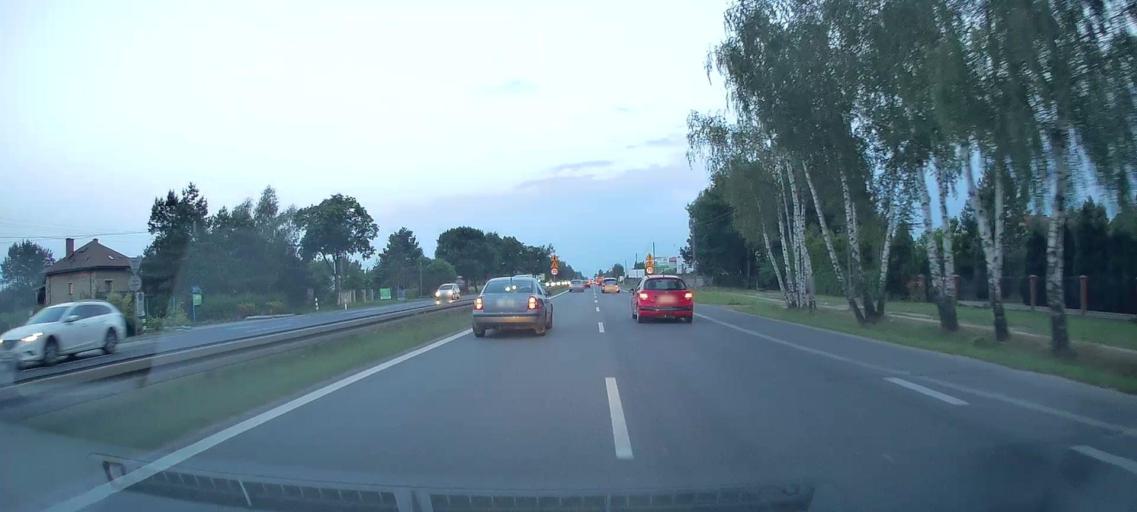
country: PL
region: Masovian Voivodeship
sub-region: Powiat pruszkowski
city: Nadarzyn
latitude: 52.0551
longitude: 20.8676
